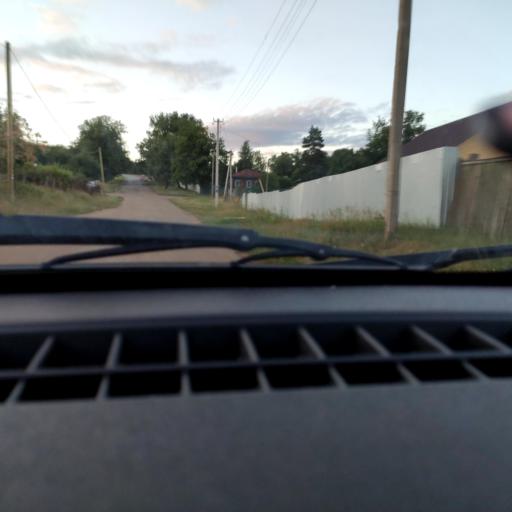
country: RU
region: Bashkortostan
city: Avdon
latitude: 54.6374
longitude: 55.5911
